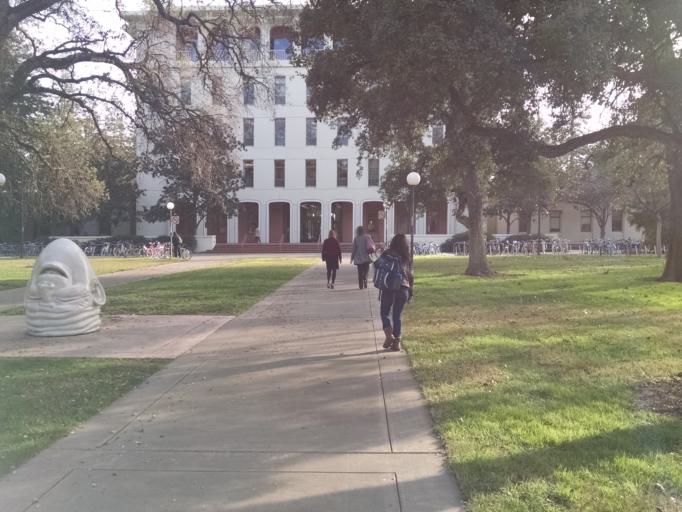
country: US
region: California
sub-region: Yolo County
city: Davis
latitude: 38.5378
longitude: -121.7495
